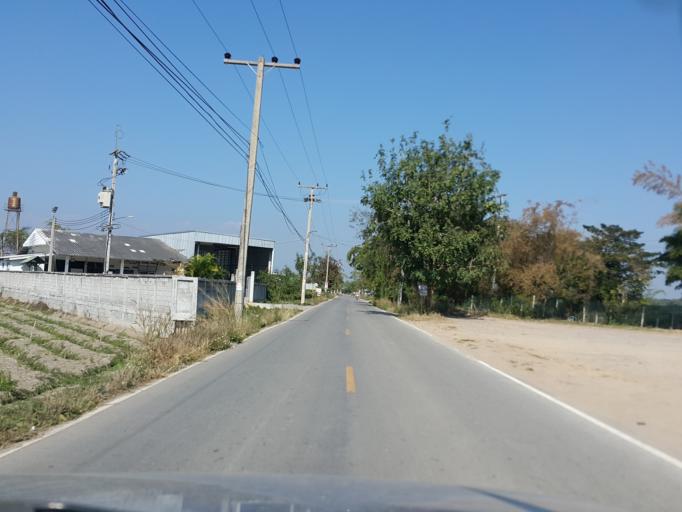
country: TH
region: Chiang Mai
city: Mae Wang
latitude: 18.5940
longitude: 98.7986
